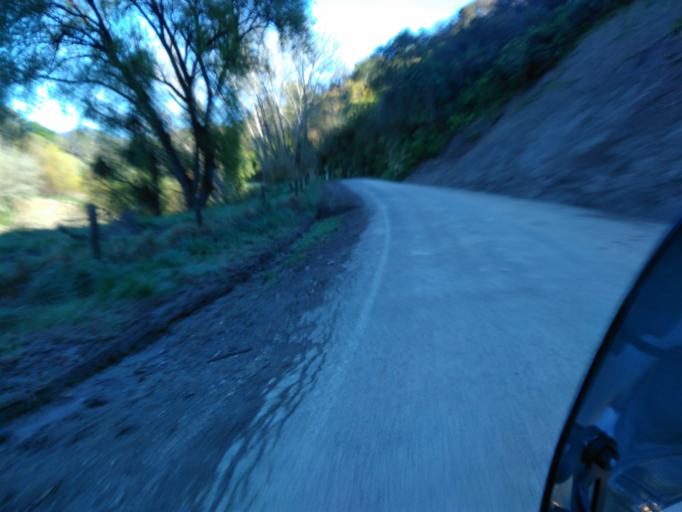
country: NZ
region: Gisborne
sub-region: Gisborne District
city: Gisborne
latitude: -38.4520
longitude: 177.7678
